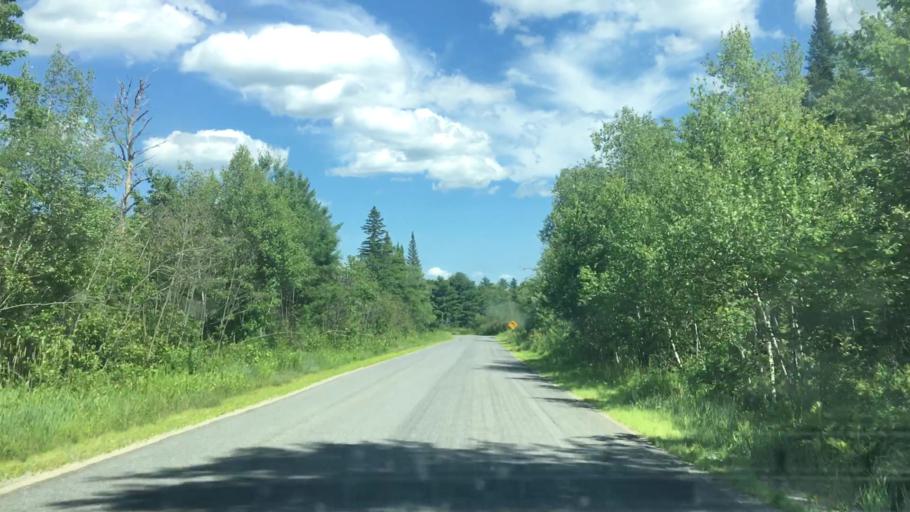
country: US
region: Maine
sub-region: Franklin County
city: Chesterville
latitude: 44.5528
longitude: -70.0991
